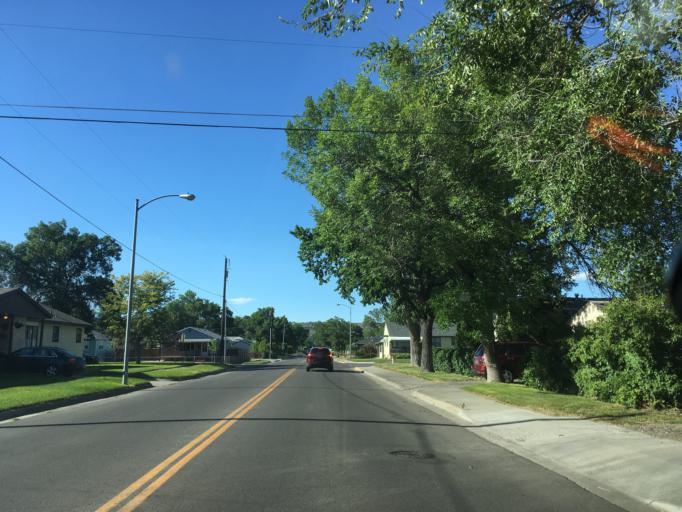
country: US
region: Montana
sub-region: Yellowstone County
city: Billings
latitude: 45.7782
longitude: -108.5641
